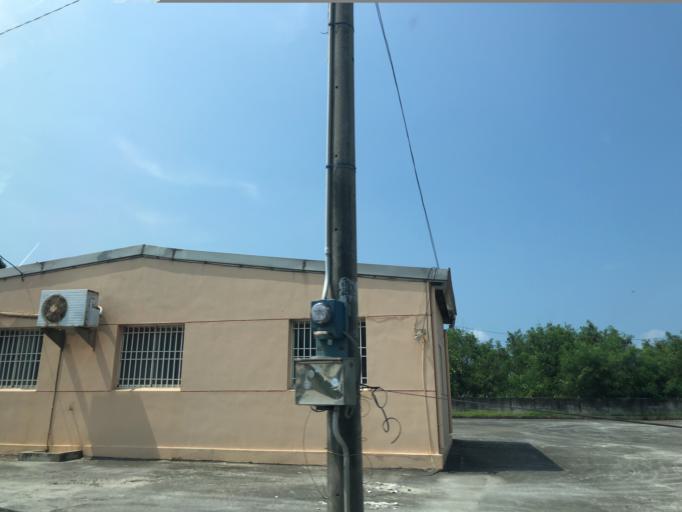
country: TW
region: Taiwan
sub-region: Chiayi
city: Taibao
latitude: 23.4603
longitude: 120.1509
